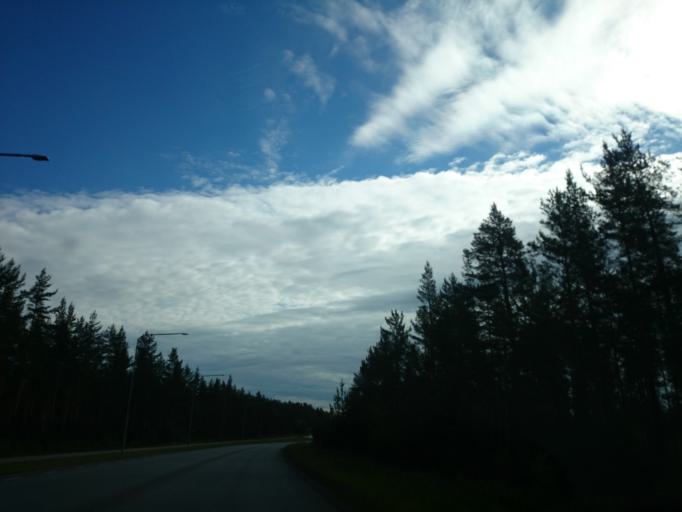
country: SE
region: Vaesternorrland
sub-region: Timra Kommun
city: Timra
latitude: 62.5007
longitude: 17.3384
